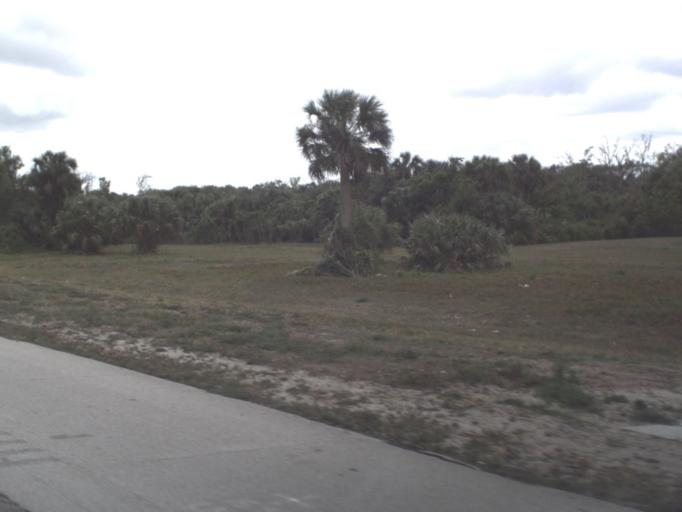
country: US
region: Florida
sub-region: Brevard County
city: South Patrick Shores
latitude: 28.1897
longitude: -80.7071
